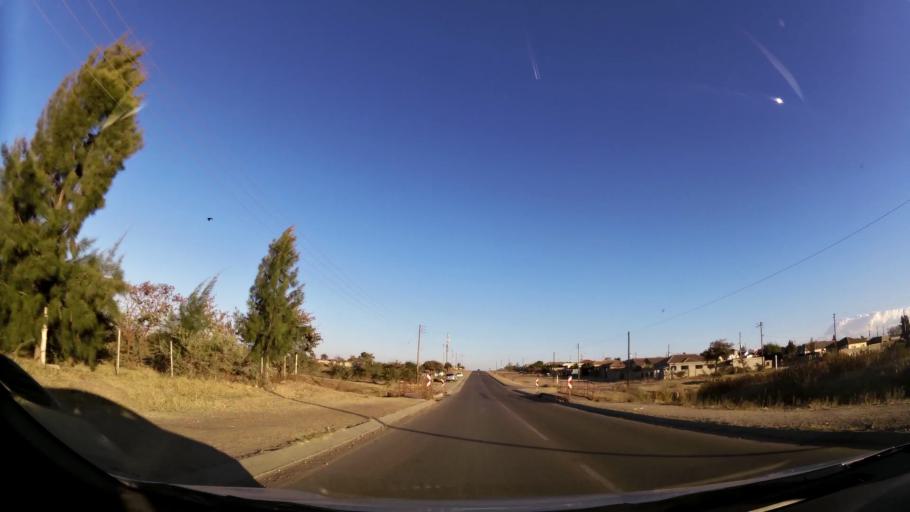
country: ZA
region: Limpopo
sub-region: Capricorn District Municipality
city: Polokwane
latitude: -23.8426
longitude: 29.3528
